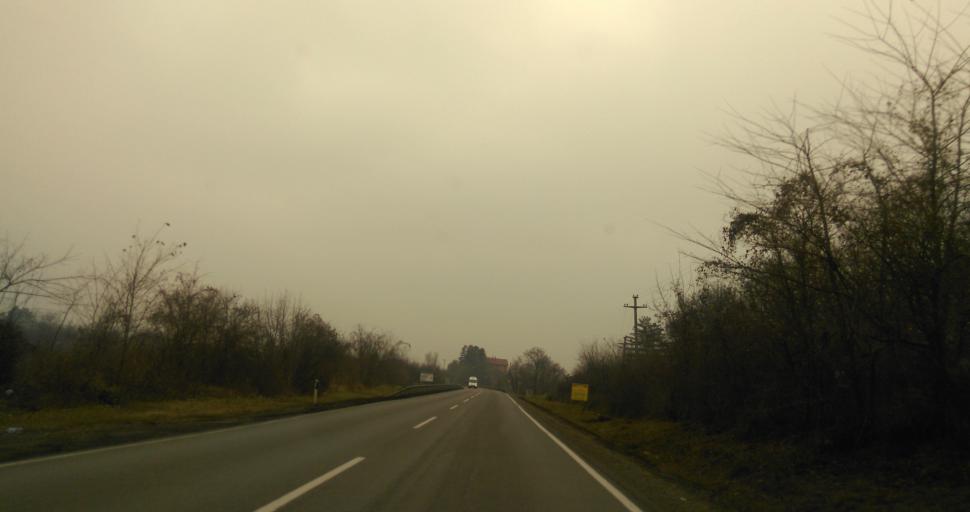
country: RS
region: Central Serbia
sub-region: Belgrade
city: Zvezdara
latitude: 44.7179
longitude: 20.5098
